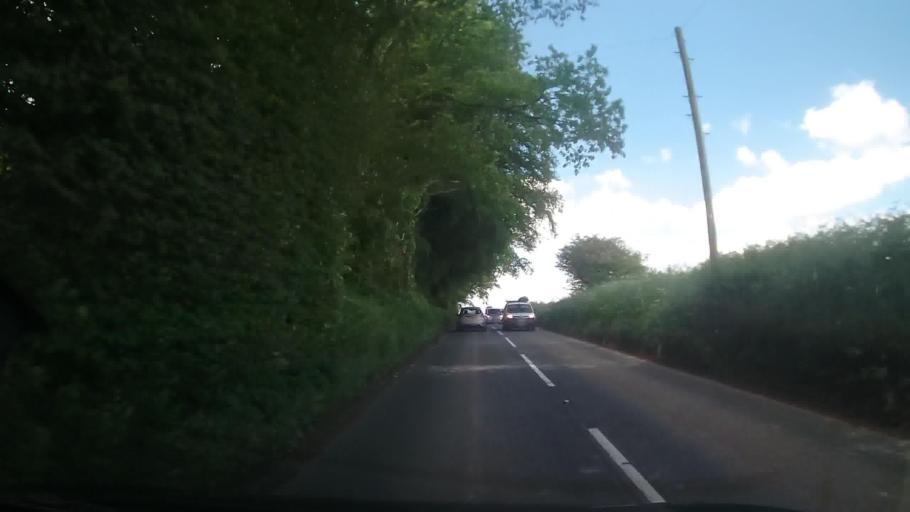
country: GB
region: England
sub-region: Devon
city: Dartmouth
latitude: 50.3558
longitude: -3.6537
